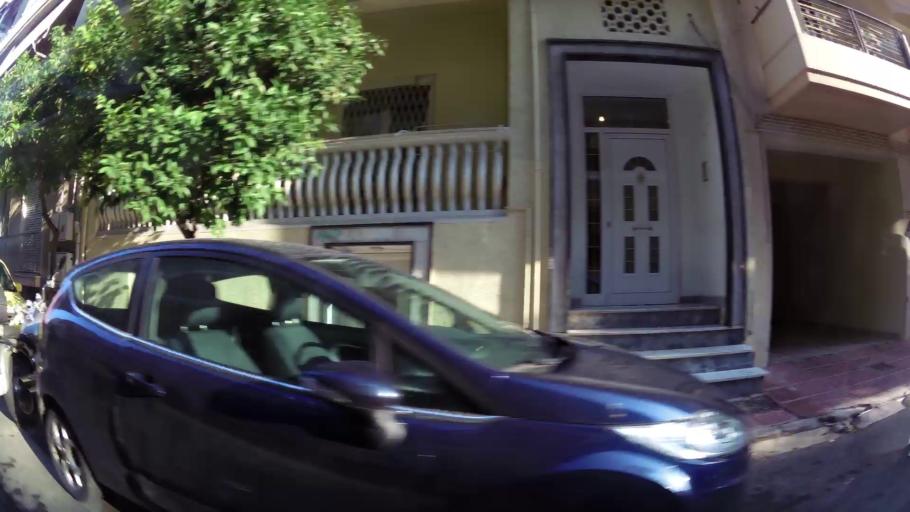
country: GR
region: Attica
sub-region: Nomarchia Athinas
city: Kaisariani
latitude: 37.9784
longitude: 23.7601
